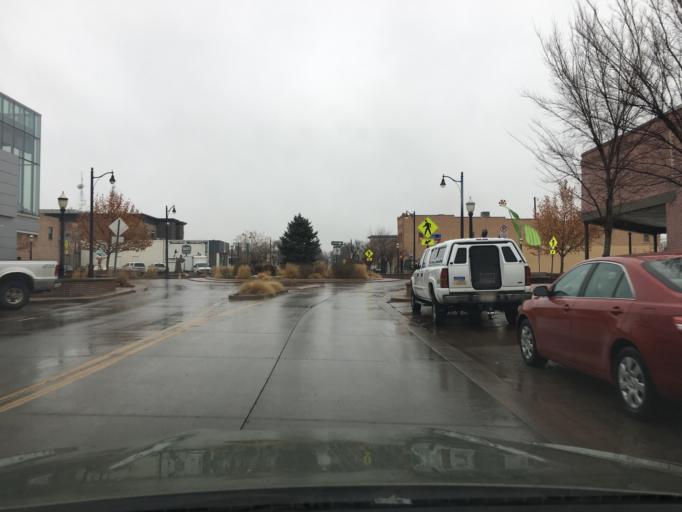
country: US
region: Colorado
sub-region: Mesa County
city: Grand Junction
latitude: 39.0669
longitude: -108.5610
